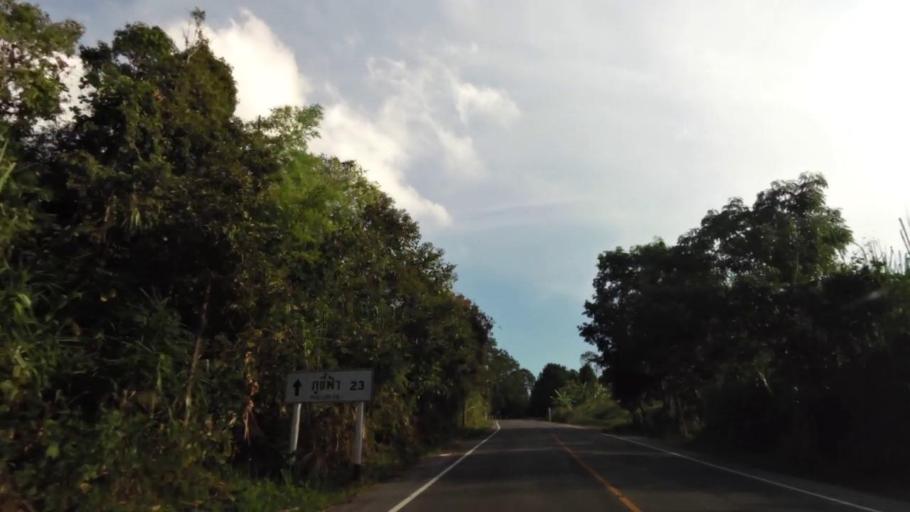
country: TH
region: Chiang Rai
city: Khun Tan
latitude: 19.8730
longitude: 100.3212
